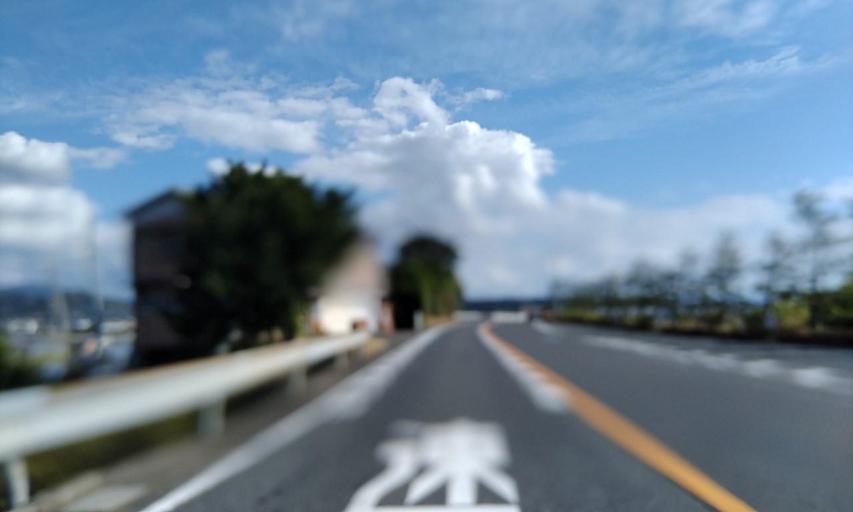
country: JP
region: Wakayama
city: Tanabe
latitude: 33.7766
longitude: 135.3101
